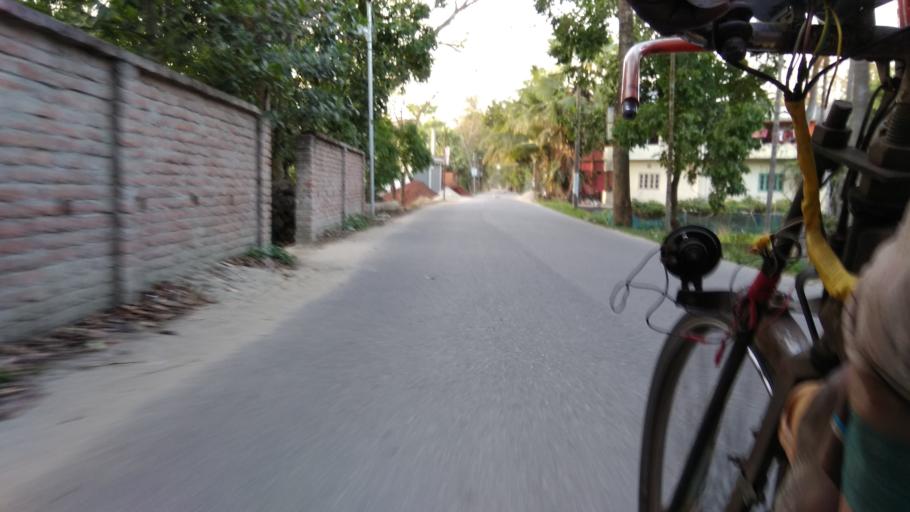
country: BD
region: Barisal
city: Mehendiganj
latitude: 22.9179
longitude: 90.4103
